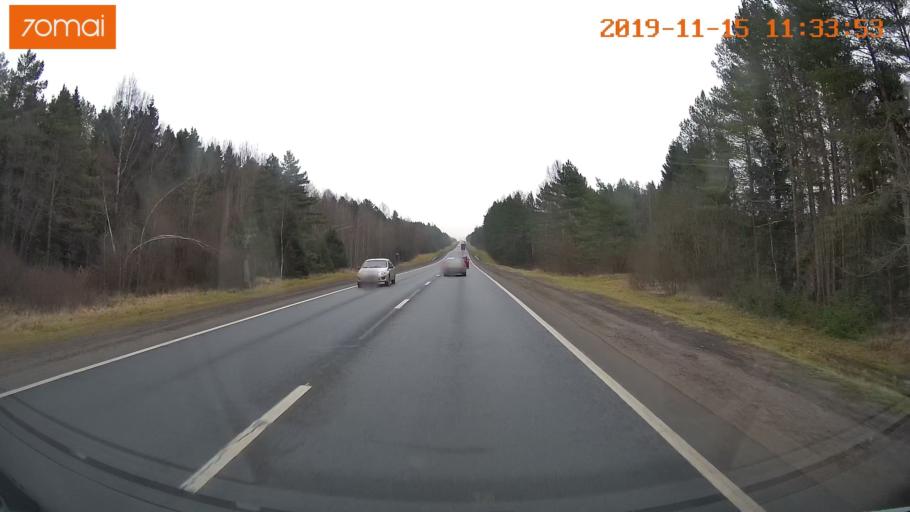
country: RU
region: Vologda
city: Molochnoye
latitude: 59.1909
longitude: 39.5999
